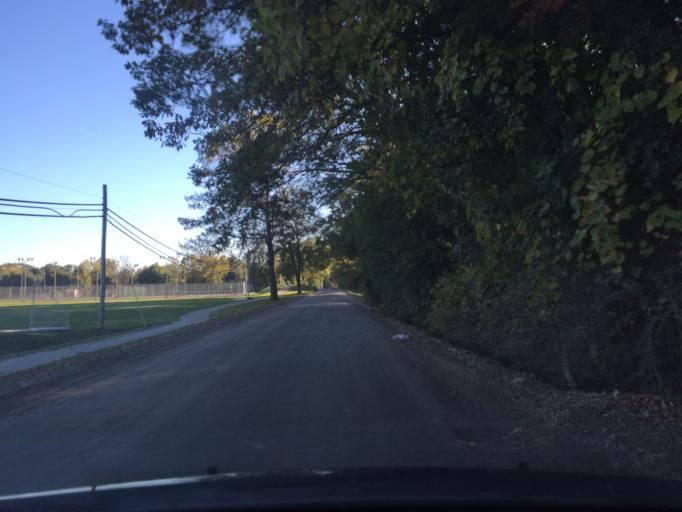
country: US
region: Michigan
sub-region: Oakland County
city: Franklin
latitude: 42.5610
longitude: -83.2948
